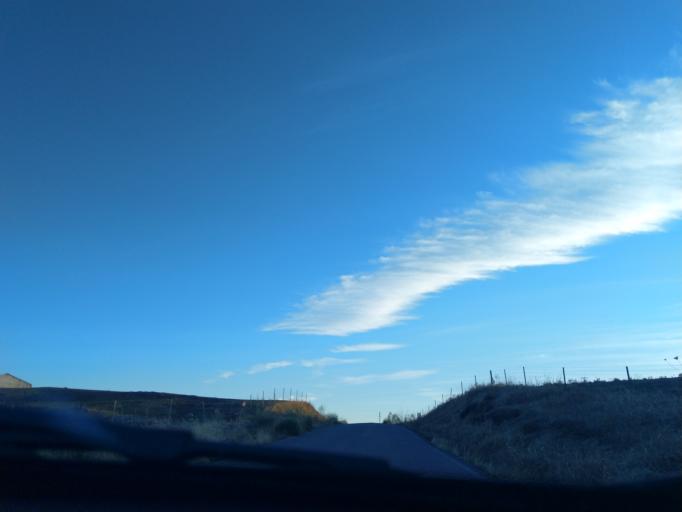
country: ES
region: Extremadura
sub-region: Provincia de Badajoz
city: Berlanga
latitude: 38.2624
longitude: -5.8255
